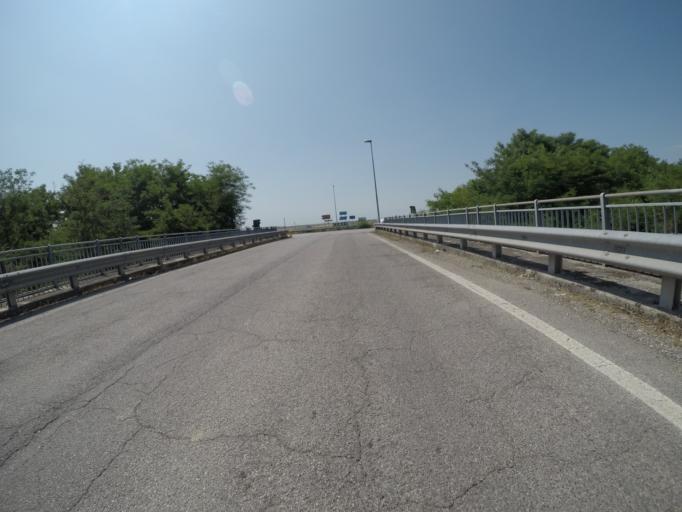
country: IT
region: Veneto
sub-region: Provincia di Rovigo
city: Pincara
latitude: 45.0024
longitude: 11.6317
